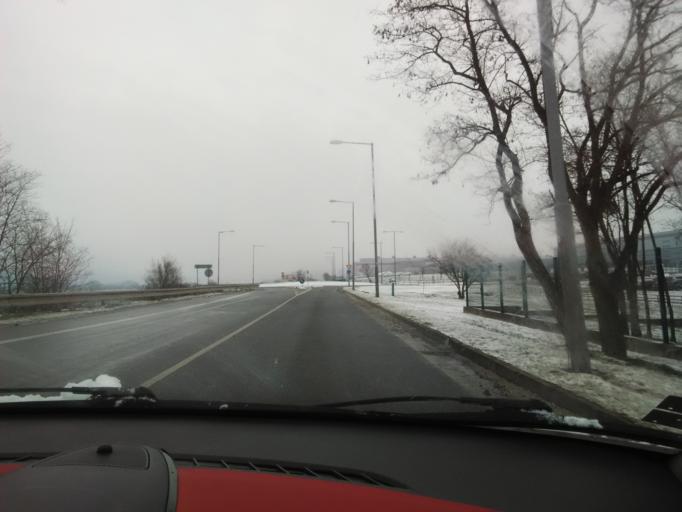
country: SK
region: Bratislavsky
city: Stupava
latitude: 48.2384
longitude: 16.9931
